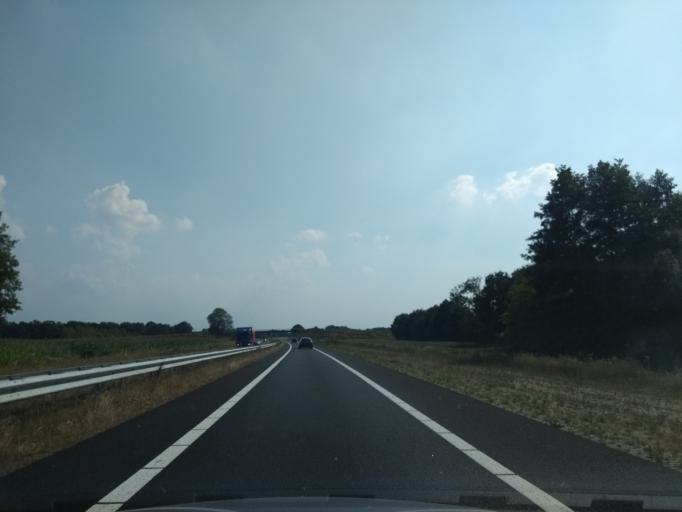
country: NL
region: Overijssel
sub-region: Gemeente Haaksbergen
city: Haaksbergen
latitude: 52.1488
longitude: 6.6829
